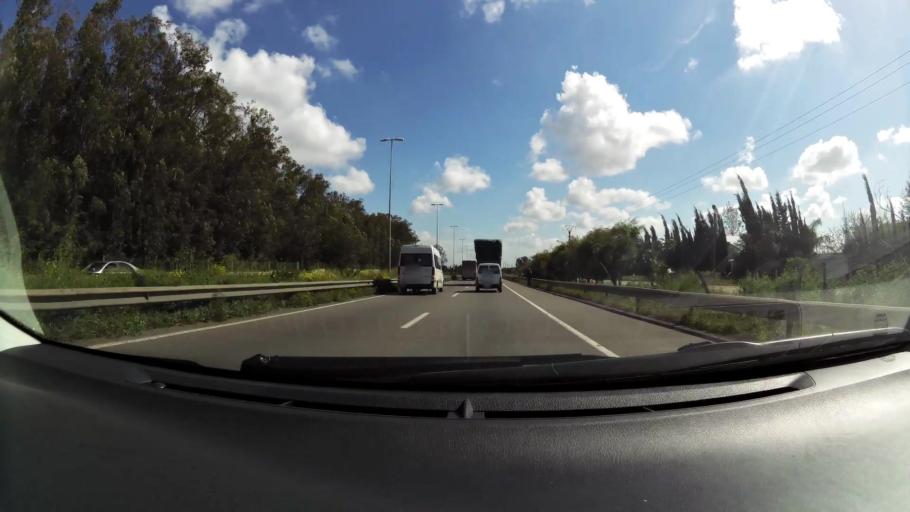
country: MA
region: Grand Casablanca
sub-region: Nouaceur
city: Bouskoura
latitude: 33.4705
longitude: -7.6334
